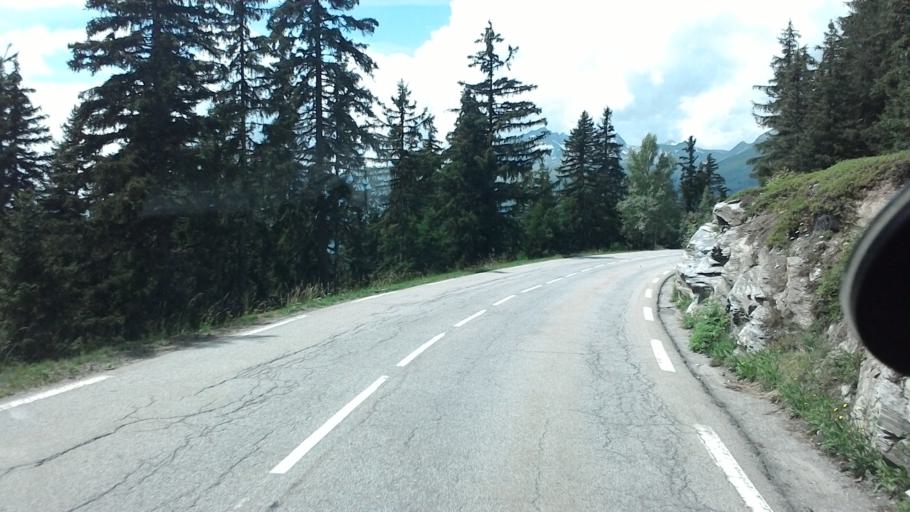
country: FR
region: Rhone-Alpes
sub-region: Departement de la Savoie
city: Seez
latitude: 45.6231
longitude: 6.8431
